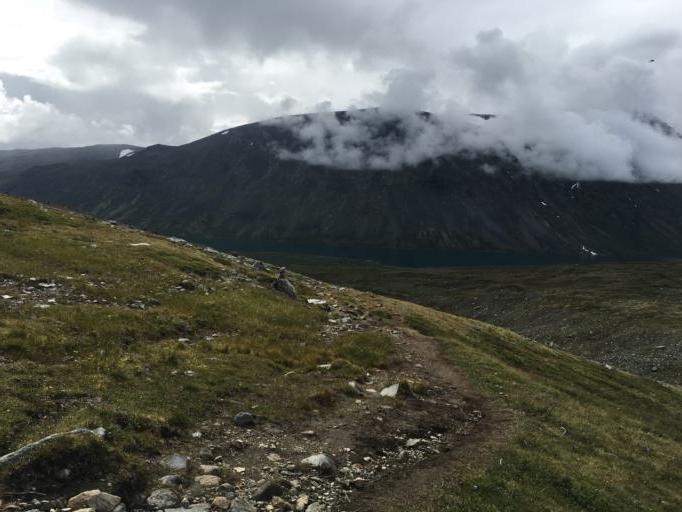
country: NO
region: Oppland
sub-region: Lom
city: Fossbergom
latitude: 61.5718
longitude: 8.6734
